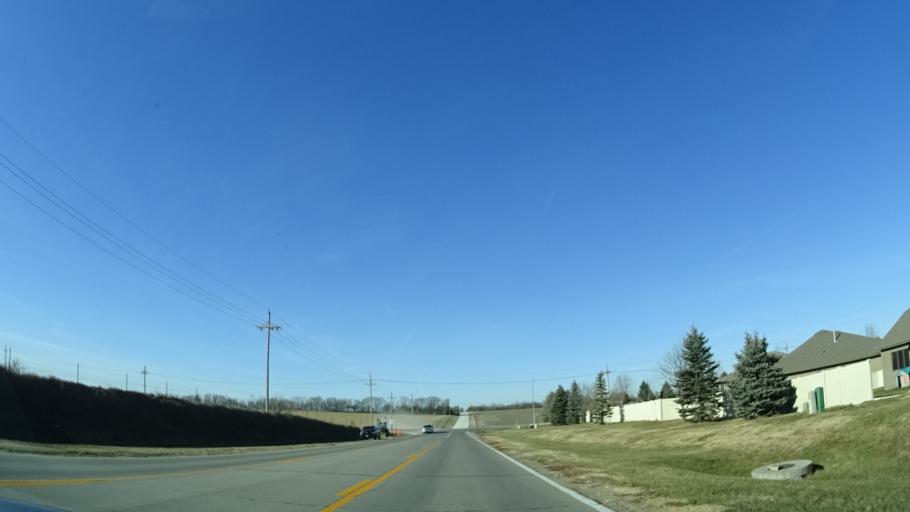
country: US
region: Nebraska
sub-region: Sarpy County
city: Papillion
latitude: 41.1180
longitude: -96.0410
